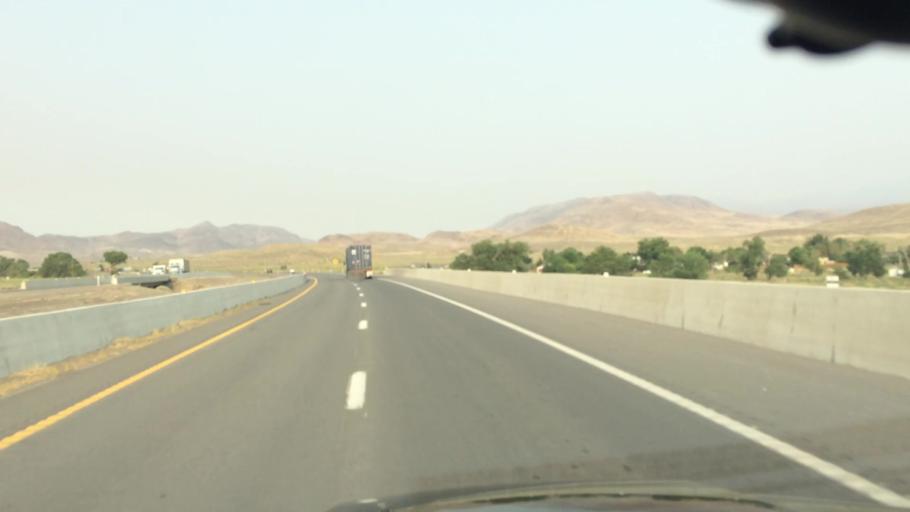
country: US
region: Nevada
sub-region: Lyon County
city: Fernley
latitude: 39.6167
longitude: -119.3074
